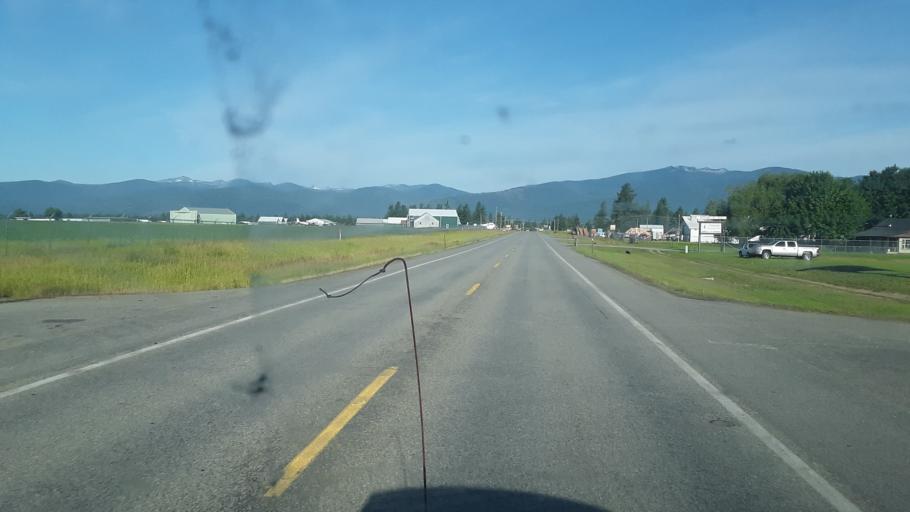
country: US
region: Idaho
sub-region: Boundary County
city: Bonners Ferry
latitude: 48.7314
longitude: -116.2867
